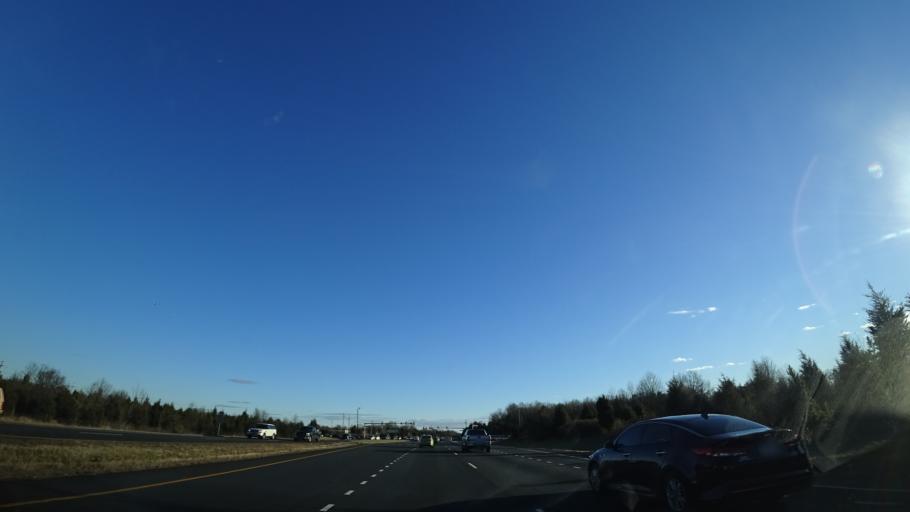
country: US
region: Virginia
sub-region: Prince William County
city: Bull Run
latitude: 38.7679
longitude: -77.5360
